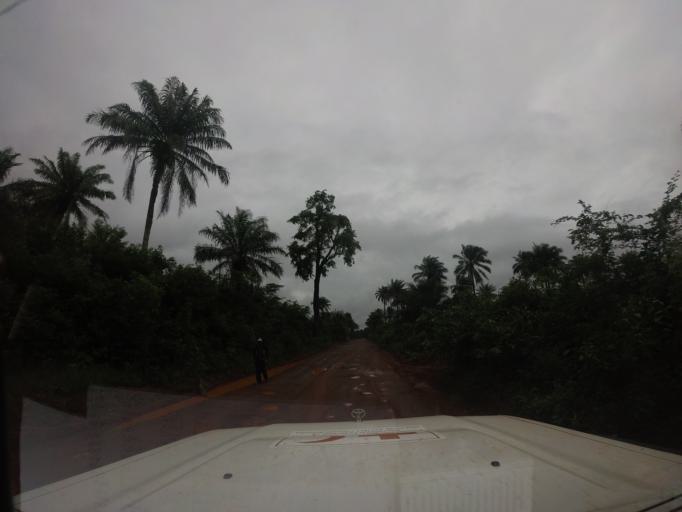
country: SL
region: Northern Province
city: Kambia
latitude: 9.1714
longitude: -12.8779
